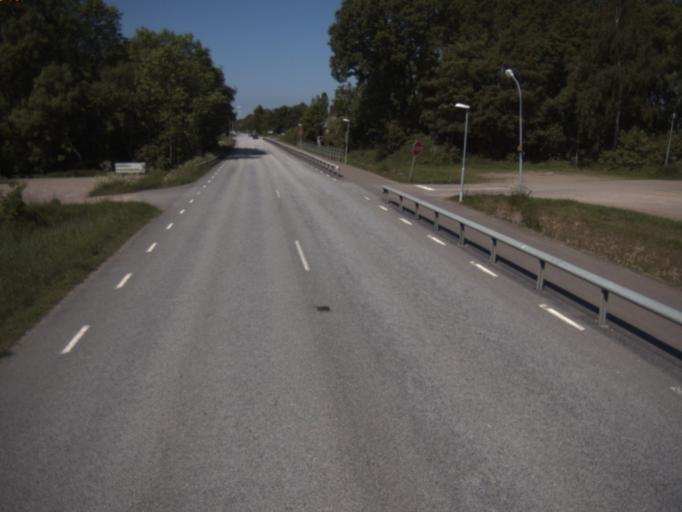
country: SE
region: Skane
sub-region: Helsingborg
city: Rydeback
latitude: 56.0024
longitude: 12.7668
